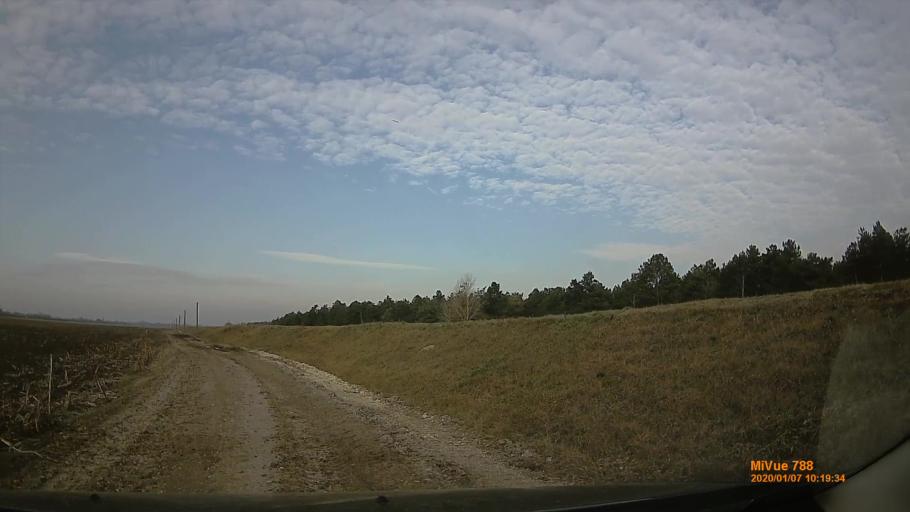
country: HU
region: Gyor-Moson-Sopron
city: Rajka
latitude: 47.9206
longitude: 17.1971
